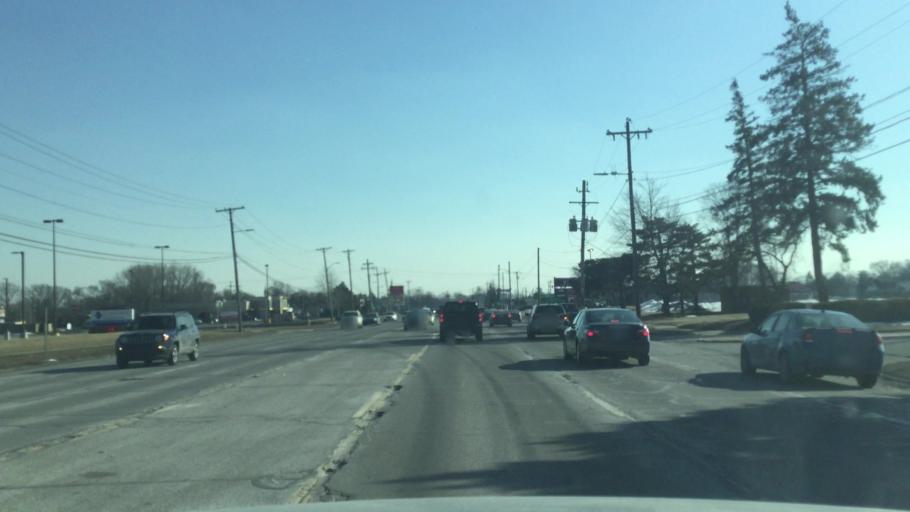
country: US
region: Michigan
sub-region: Wayne County
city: Westland
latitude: 42.3415
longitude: -83.3851
